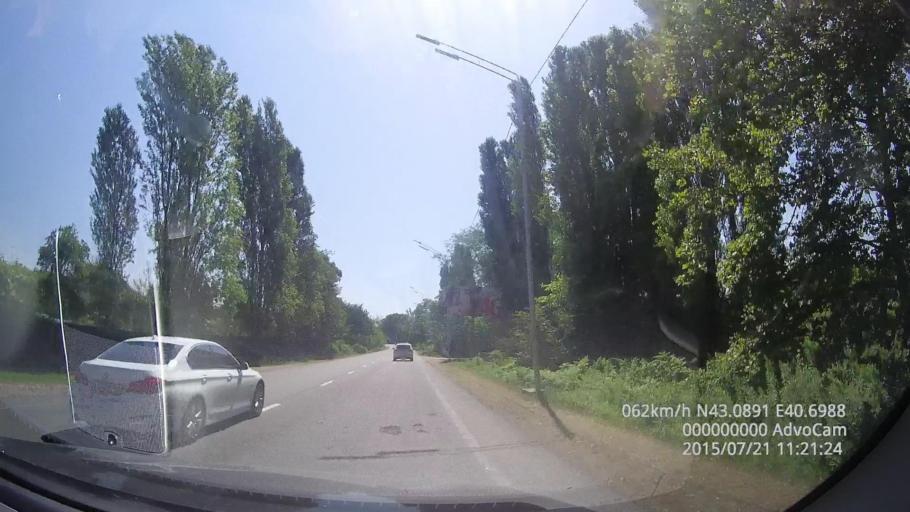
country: GE
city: P'rimorsk'oe
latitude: 43.0890
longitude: 40.6992
